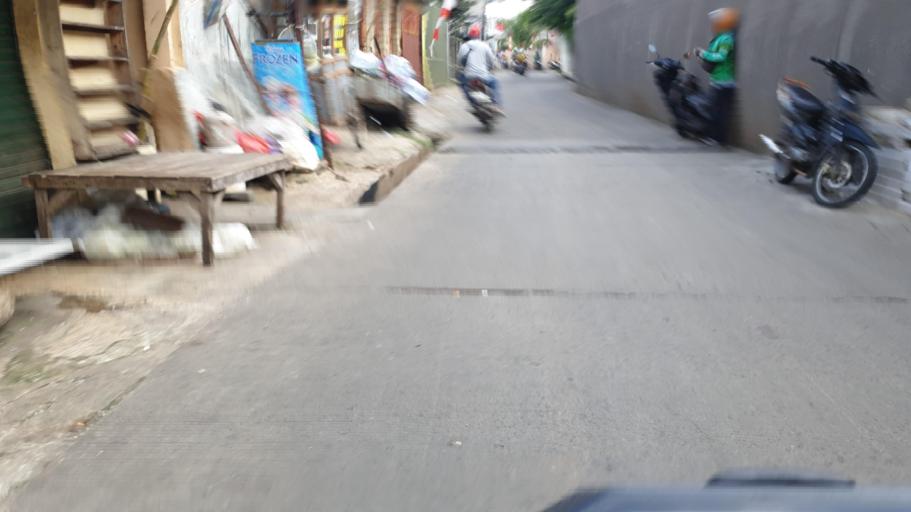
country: ID
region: West Java
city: Depok
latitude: -6.3670
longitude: 106.8500
